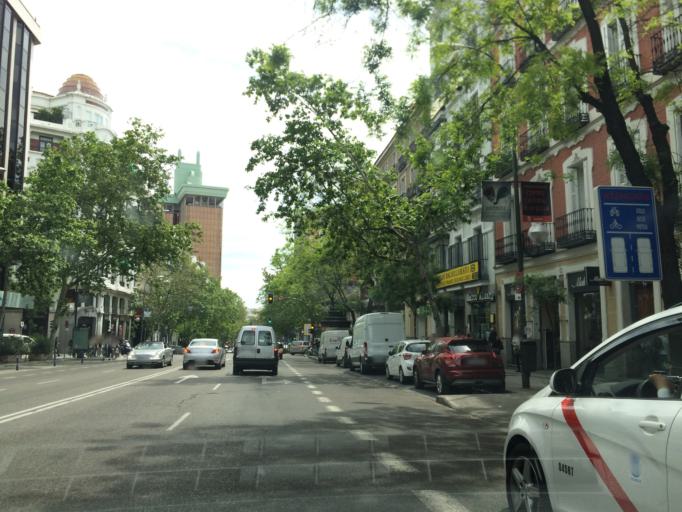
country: ES
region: Madrid
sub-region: Provincia de Madrid
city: Chamberi
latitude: 40.4271
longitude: -3.6946
